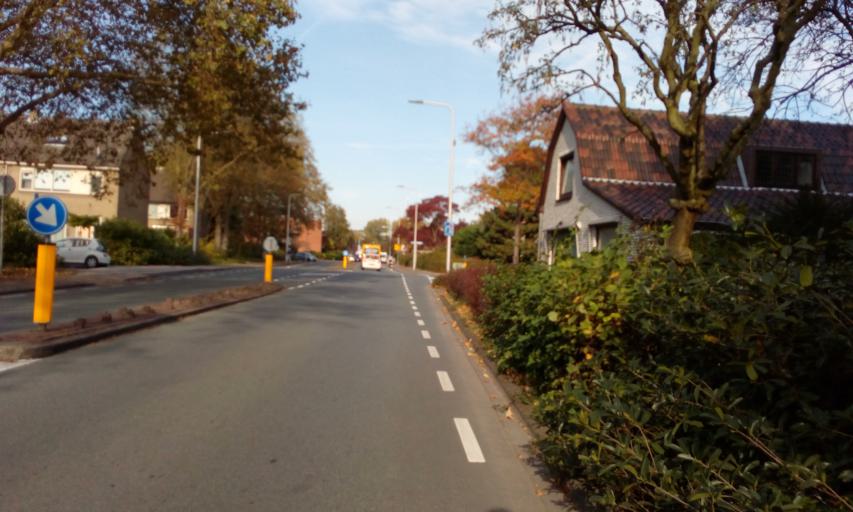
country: NL
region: South Holland
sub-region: Gemeente Westland
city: Naaldwijk
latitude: 51.9950
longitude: 4.2150
